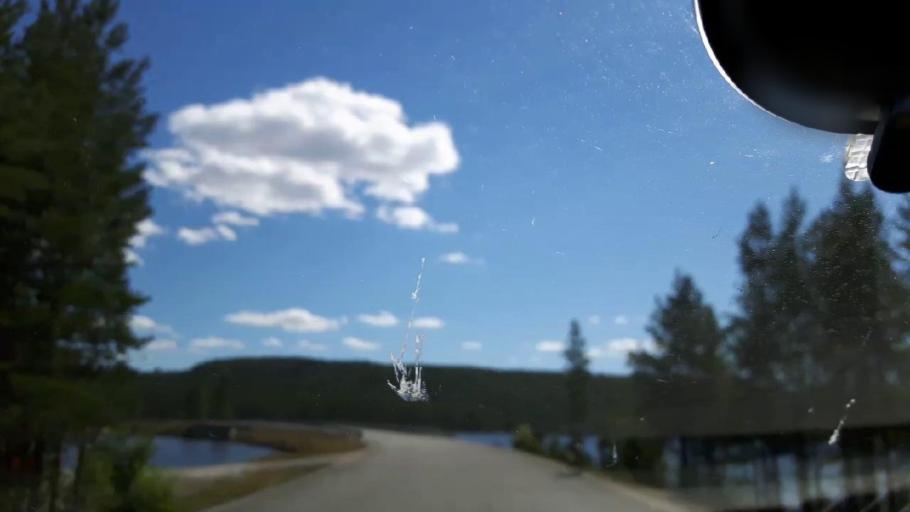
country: SE
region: Vaesternorrland
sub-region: Ange Kommun
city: Fransta
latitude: 62.6949
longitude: 16.3900
